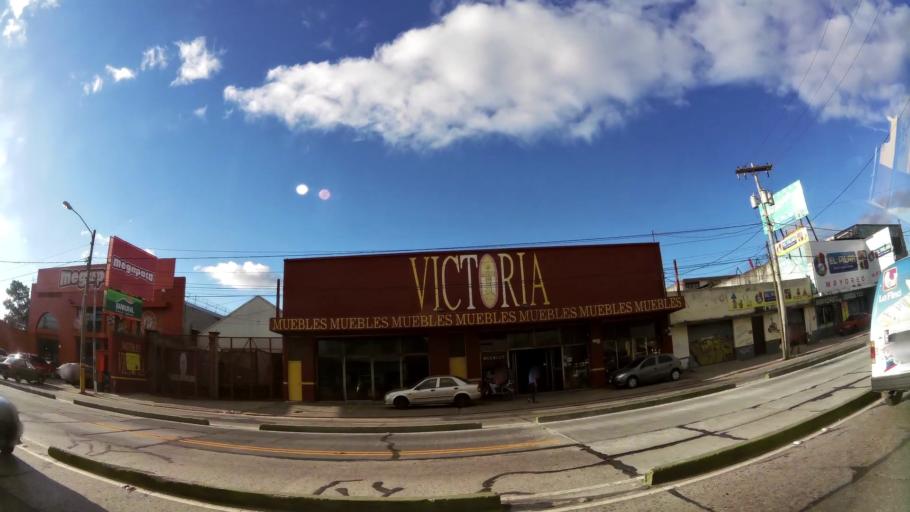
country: GT
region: Guatemala
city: Guatemala City
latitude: 14.6236
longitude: -90.5231
